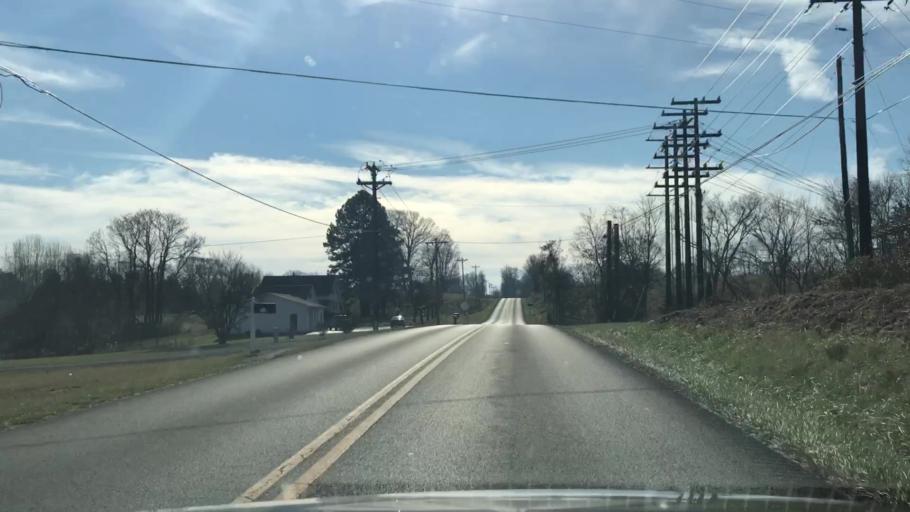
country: US
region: Kentucky
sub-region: Metcalfe County
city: Edmonton
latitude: 36.9554
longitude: -85.6138
